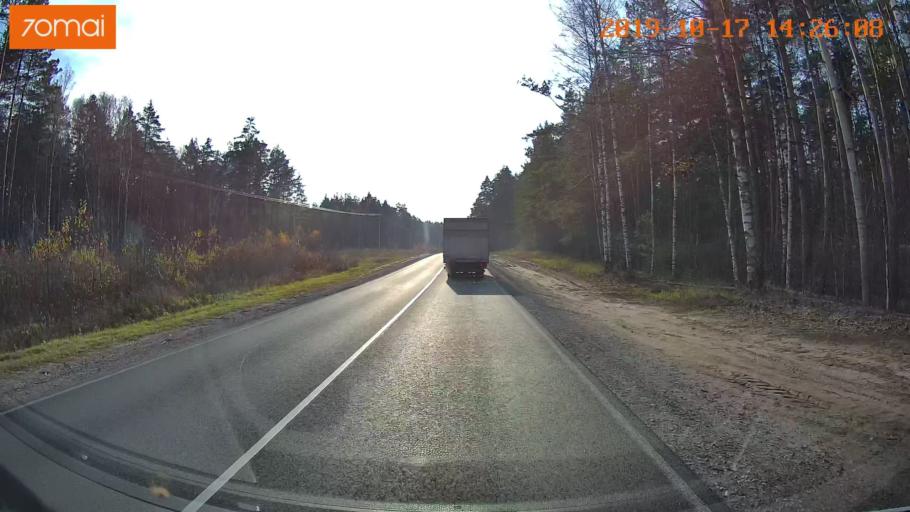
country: RU
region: Moskovskaya
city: Radovitskiy
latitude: 54.9945
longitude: 39.9710
